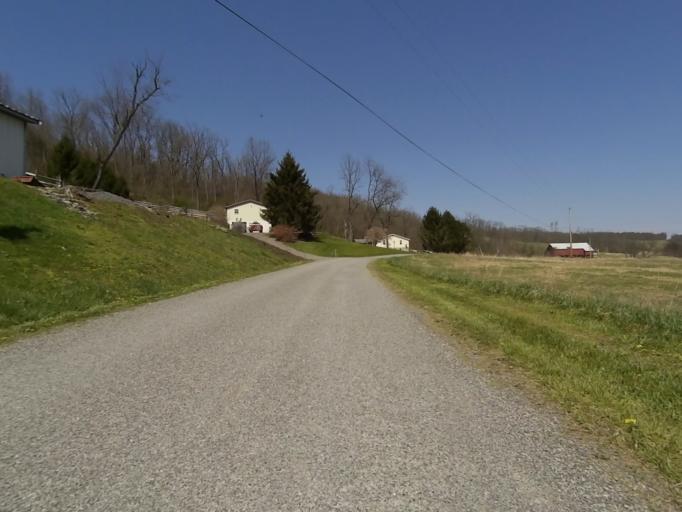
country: US
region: Pennsylvania
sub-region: Blair County
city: Williamsburg
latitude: 40.5367
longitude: -78.1646
